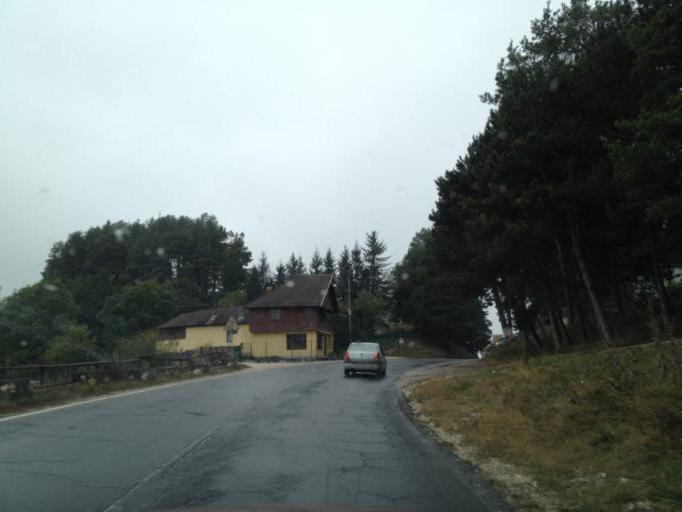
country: RO
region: Arges
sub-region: Comuna Valea Mare-Pravat
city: Valea Mare Pravat
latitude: 45.2937
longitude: 25.1402
